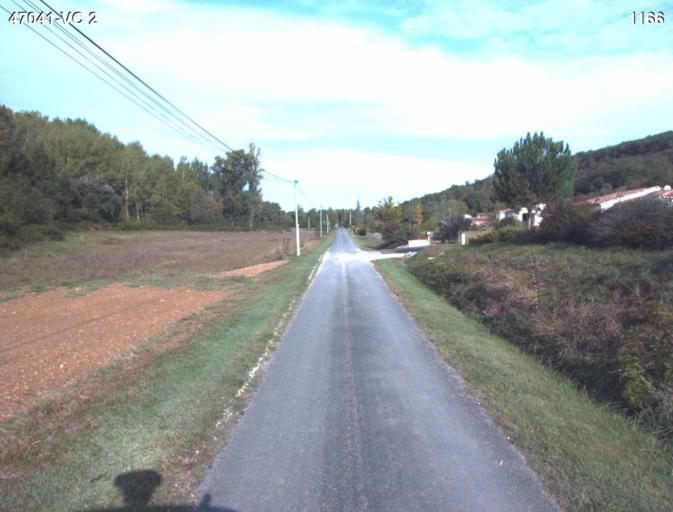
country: FR
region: Aquitaine
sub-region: Departement du Lot-et-Garonne
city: Port-Sainte-Marie
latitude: 44.1924
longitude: 0.4144
